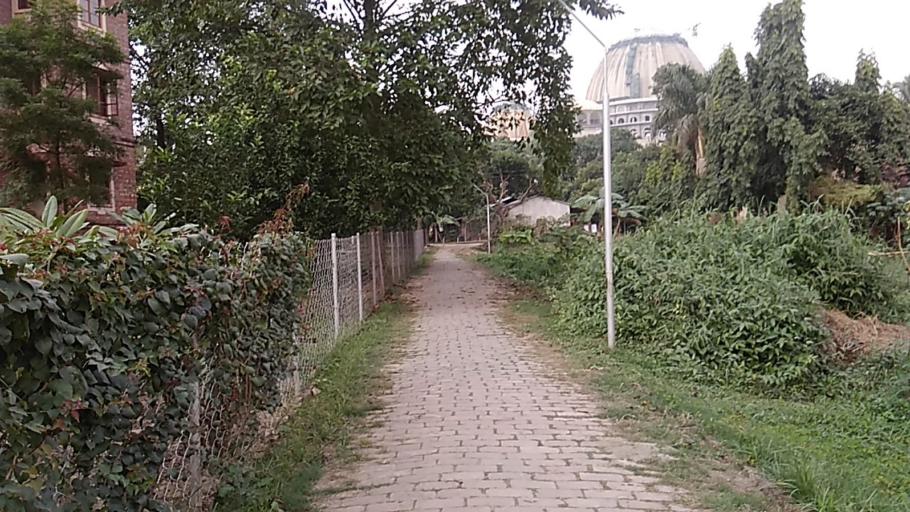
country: IN
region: West Bengal
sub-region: Nadia
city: Navadwip
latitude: 23.4218
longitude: 88.3889
